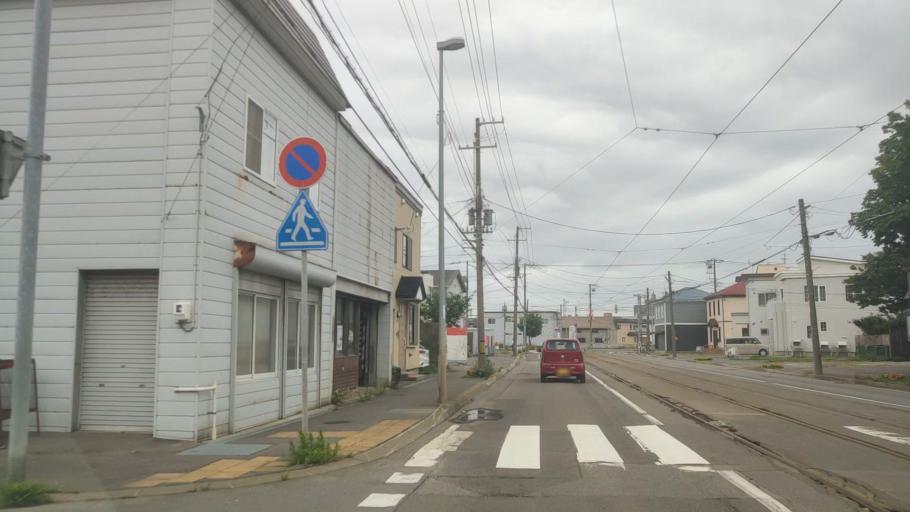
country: JP
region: Hokkaido
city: Hakodate
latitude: 41.7706
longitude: 140.7085
